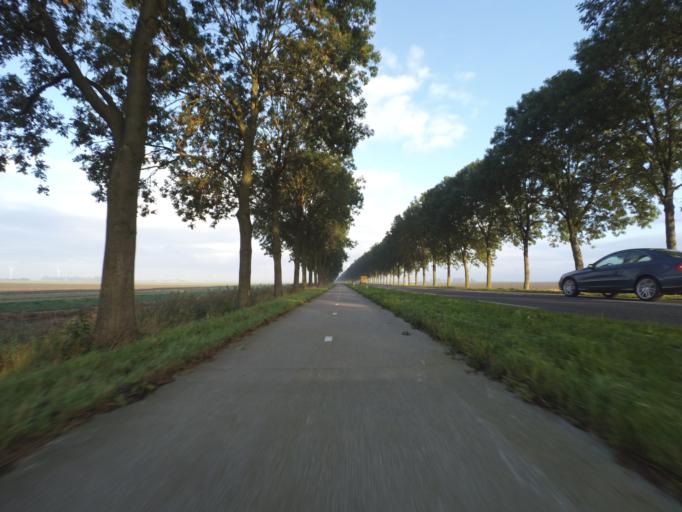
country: NL
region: Flevoland
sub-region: Gemeente Dronten
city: Biddinghuizen
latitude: 52.4638
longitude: 5.6881
